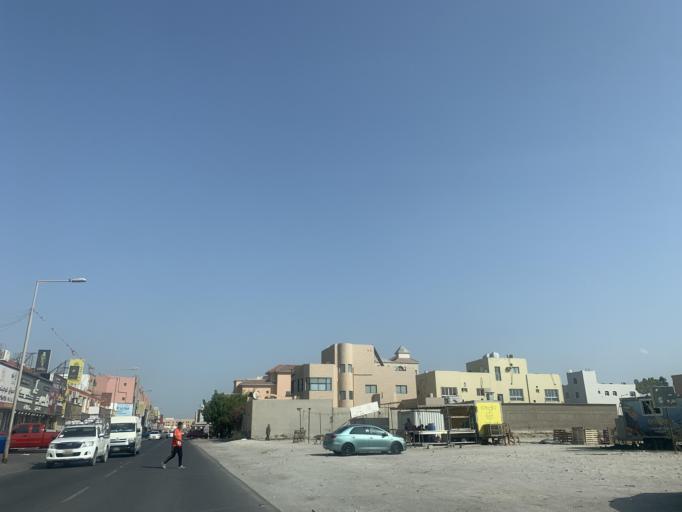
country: BH
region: Central Governorate
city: Madinat Hamad
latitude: 26.1392
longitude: 50.4912
